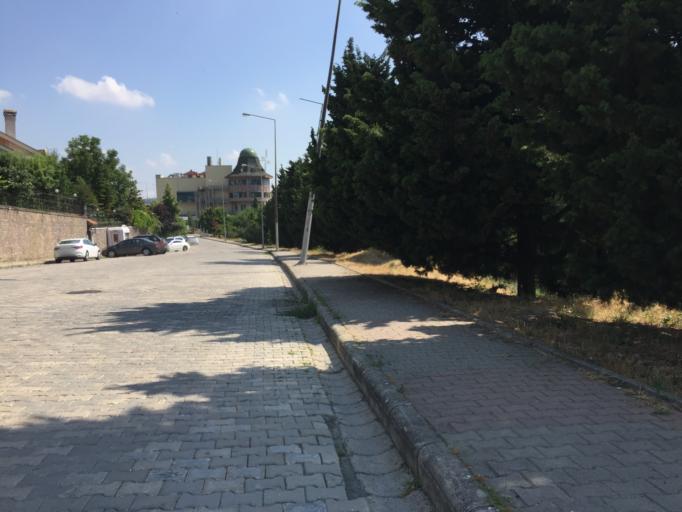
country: TR
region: Istanbul
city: Esenyurt
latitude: 41.0828
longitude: 28.6657
